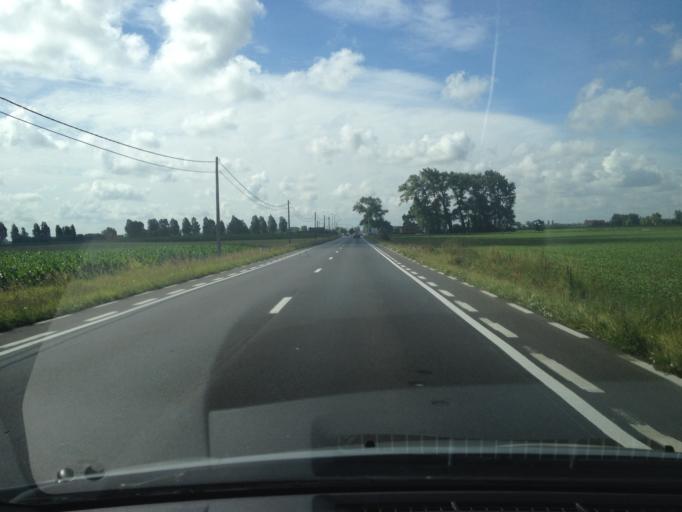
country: BE
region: Flanders
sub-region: Provincie West-Vlaanderen
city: Alveringem
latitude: 51.0107
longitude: 2.6827
